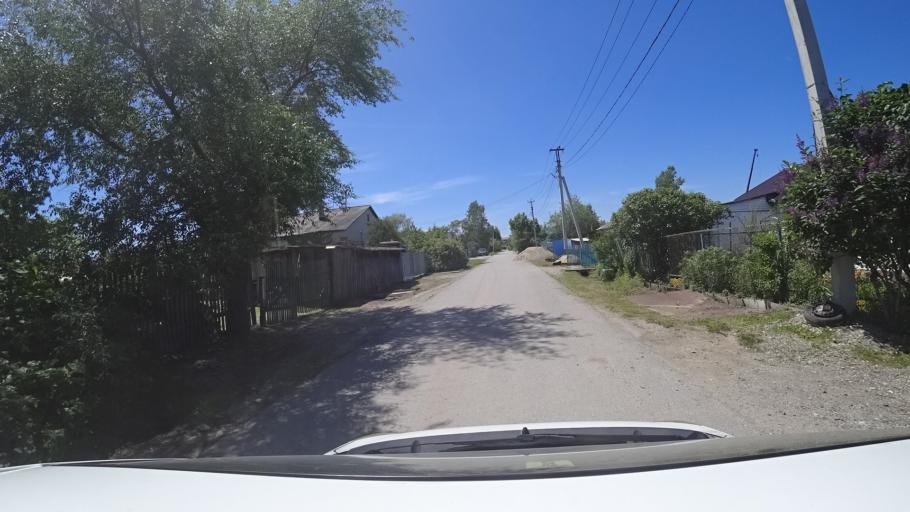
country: RU
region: Khabarovsk Krai
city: Topolevo
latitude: 48.5105
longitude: 135.1811
